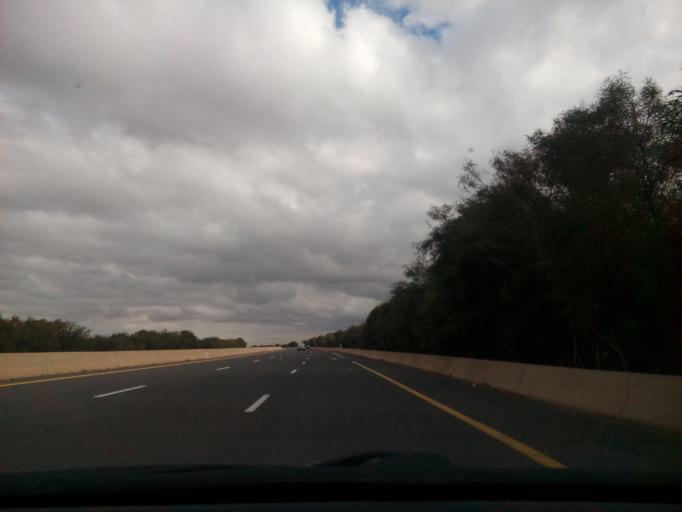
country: DZ
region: Tlemcen
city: Sidi Abdelli
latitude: 35.0192
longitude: -1.1095
